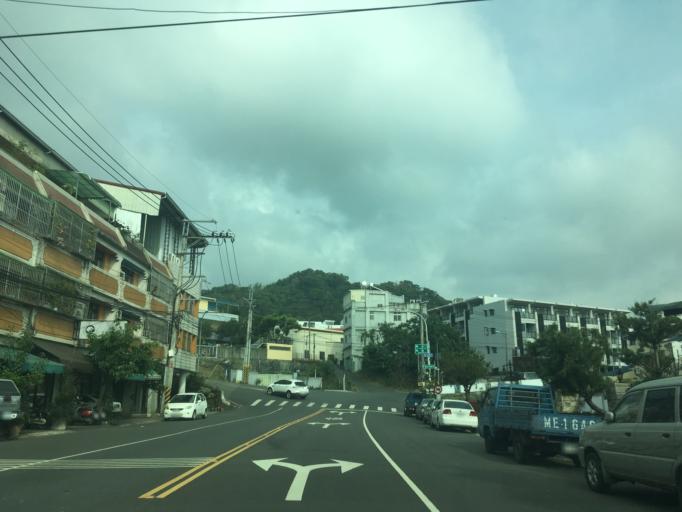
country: TW
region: Taiwan
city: Fengyuan
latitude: 24.2418
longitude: 120.7325
